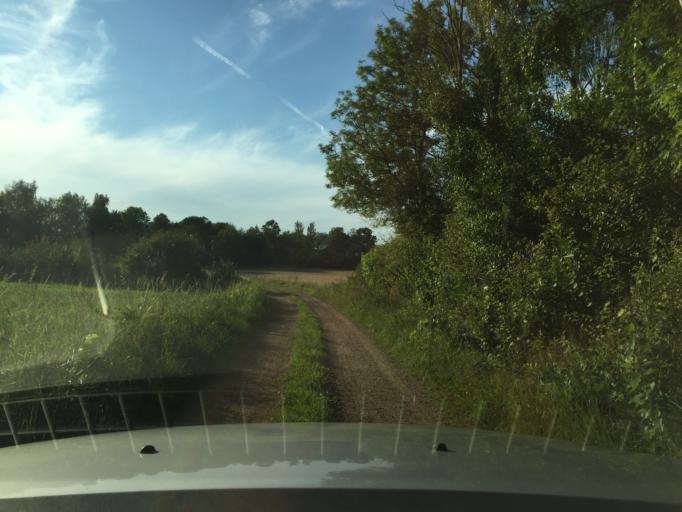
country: SE
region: Skane
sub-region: Hassleholms Kommun
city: Sosdala
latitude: 56.0251
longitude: 13.7063
